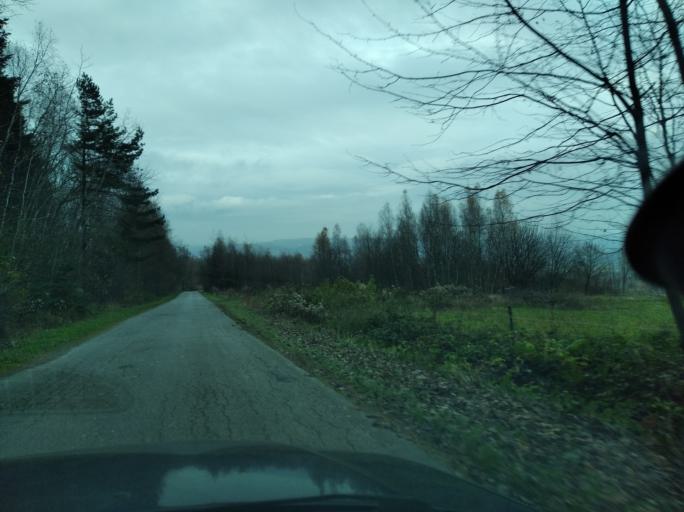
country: PL
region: Subcarpathian Voivodeship
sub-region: Powiat strzyzowski
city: Wysoka Strzyzowska
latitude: 49.8304
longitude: 21.7747
